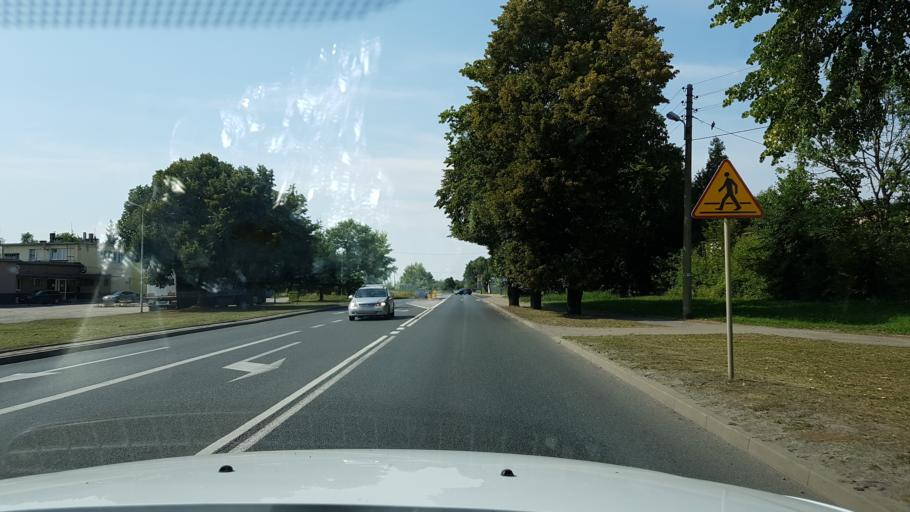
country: PL
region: West Pomeranian Voivodeship
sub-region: Powiat pyrzycki
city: Lipiany
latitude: 53.0024
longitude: 14.9544
